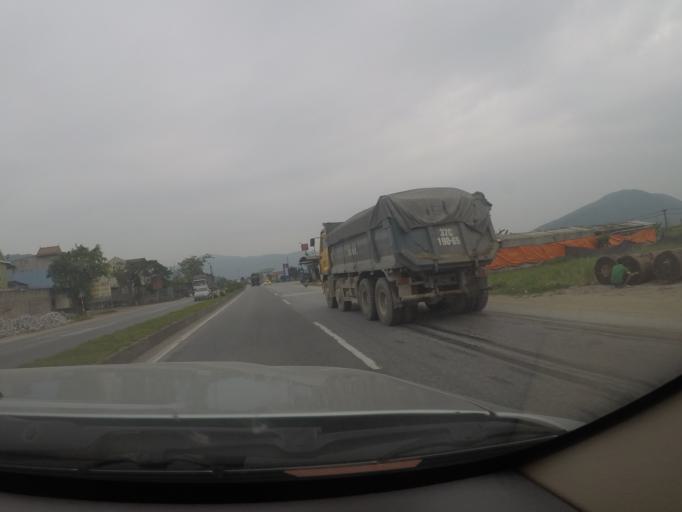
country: VN
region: Nghe An
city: Dien Chau
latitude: 18.9132
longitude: 105.6067
